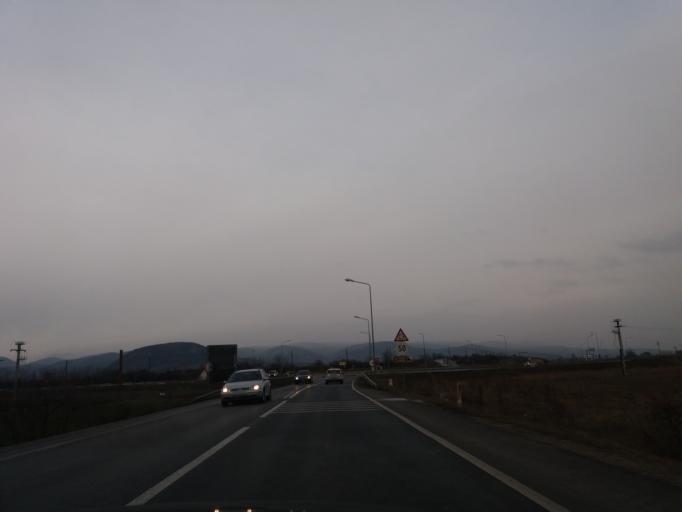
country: RO
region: Hunedoara
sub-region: Oras Simeria
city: Simeria
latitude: 45.8328
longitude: 23.0382
